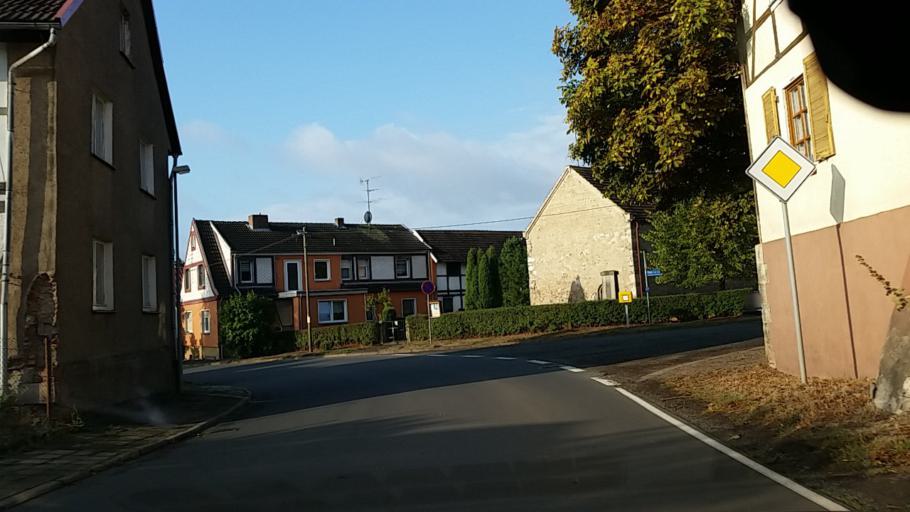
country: DE
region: Thuringia
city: Friedrichsthal
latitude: 51.5229
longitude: 10.5843
